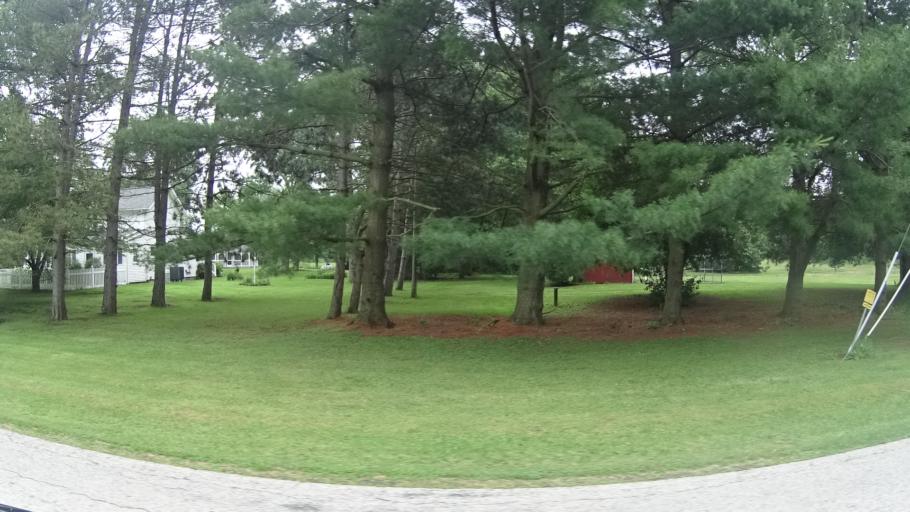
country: US
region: Ohio
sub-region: Erie County
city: Milan
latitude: 41.2892
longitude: -82.5510
